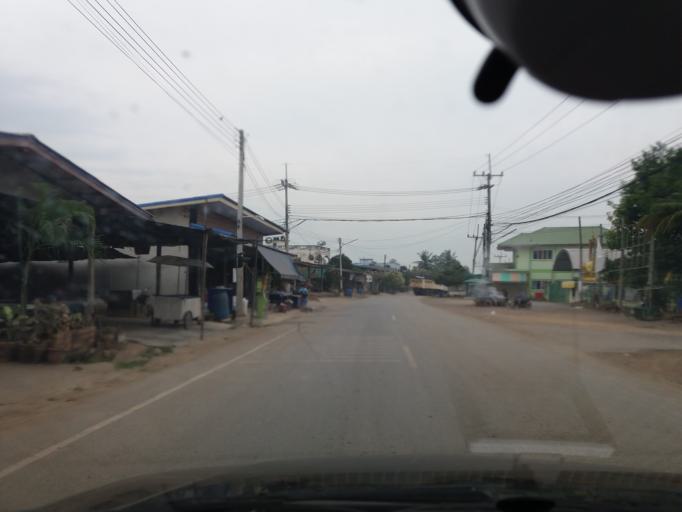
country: TH
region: Suphan Buri
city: Doembang Nangbuat
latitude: 14.8374
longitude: 100.1326
